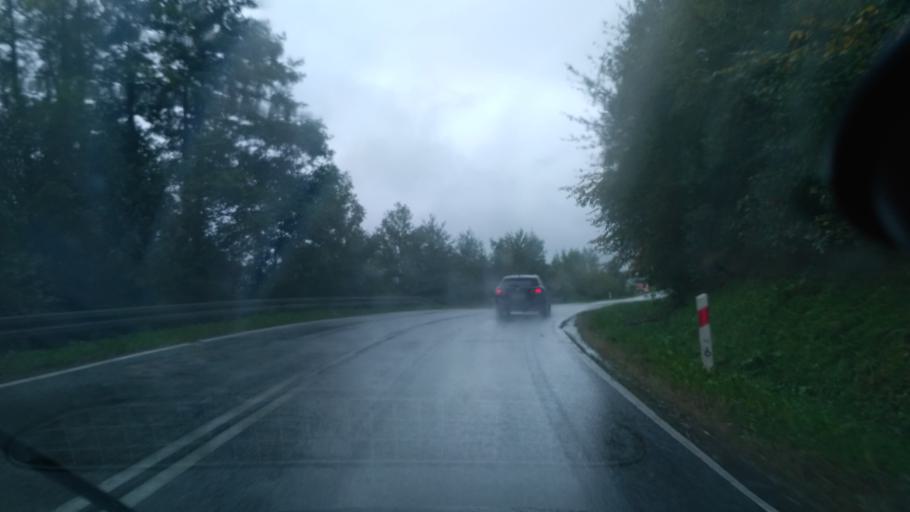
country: PL
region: Subcarpathian Voivodeship
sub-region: Powiat ropczycko-sedziszowski
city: Niedzwiada
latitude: 49.9786
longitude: 21.5596
